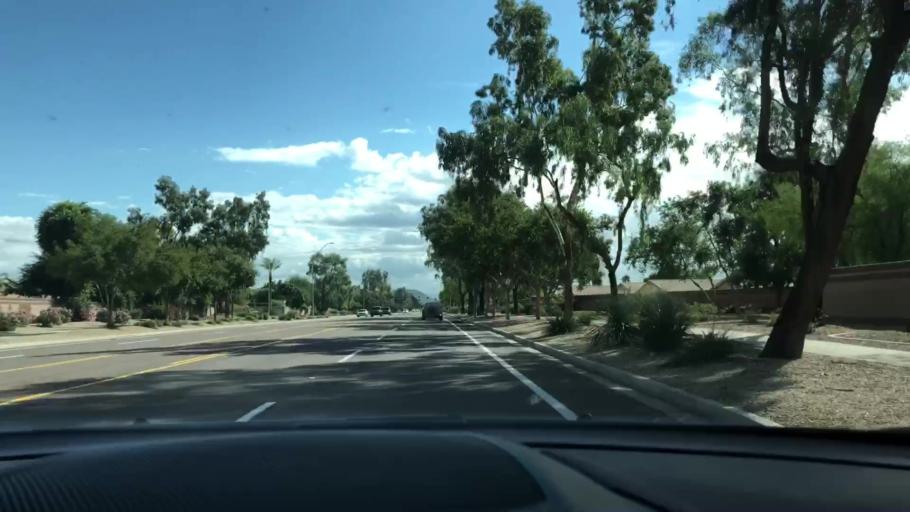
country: US
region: Arizona
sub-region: Maricopa County
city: Sun City
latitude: 33.6815
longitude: -112.2330
